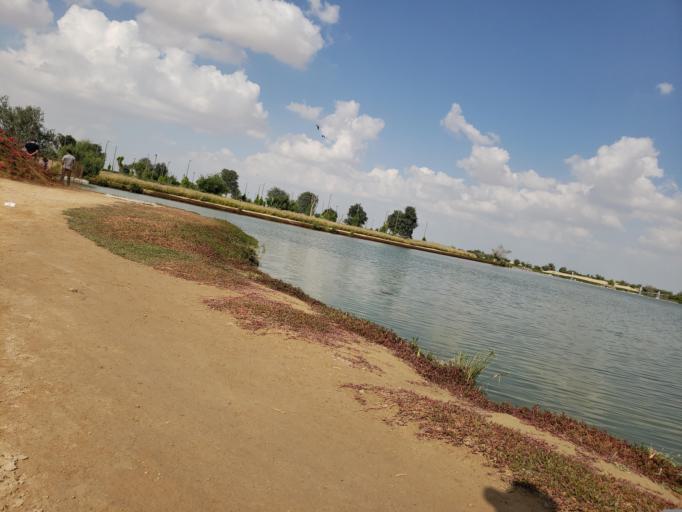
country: AE
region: Dubai
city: Dubai
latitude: 24.8538
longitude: 55.2501
